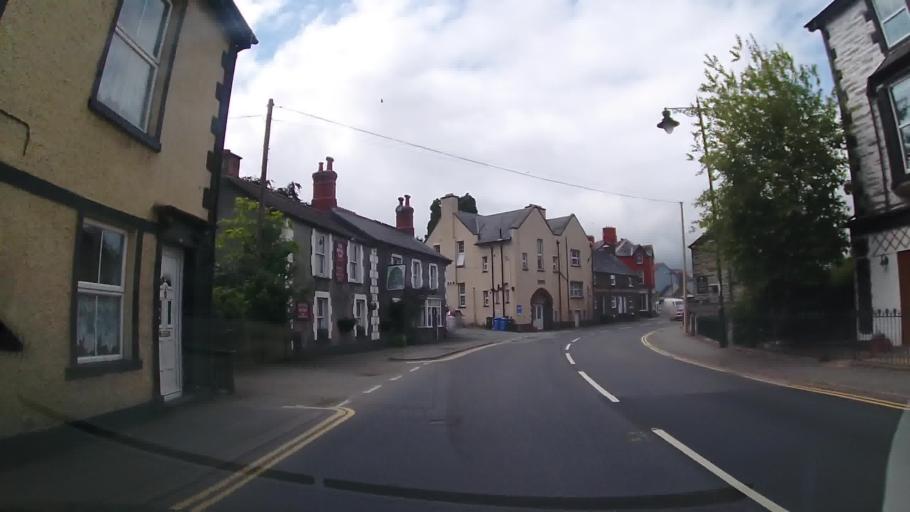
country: GB
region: Wales
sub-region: Denbighshire
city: Corwen
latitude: 52.9791
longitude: -3.3713
